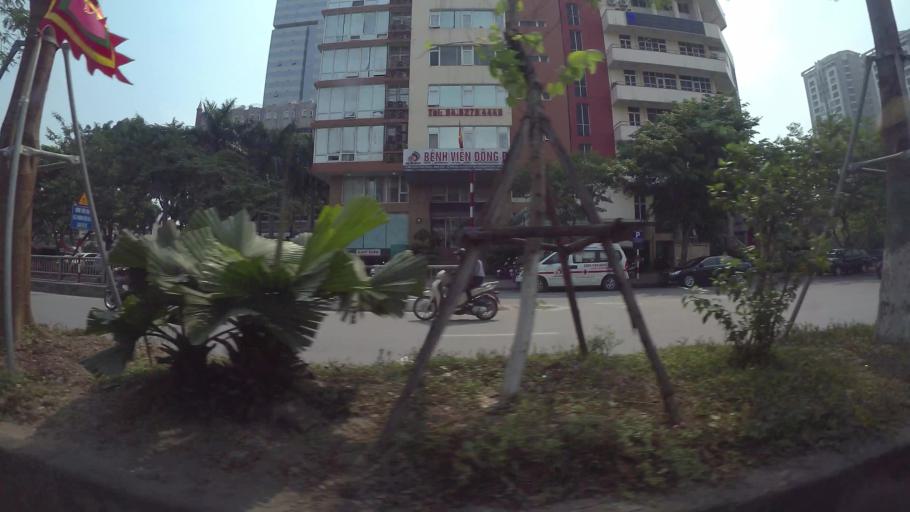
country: VN
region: Ha Noi
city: Hai BaTrung
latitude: 21.0096
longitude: 105.8382
